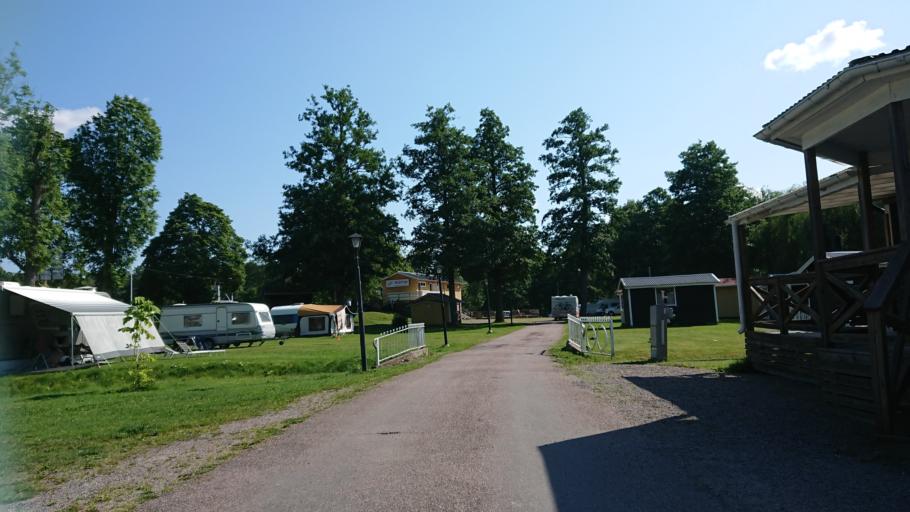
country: SE
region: Uppsala
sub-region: Osthammars Kommun
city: Osterbybruk
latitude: 60.1965
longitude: 17.9128
